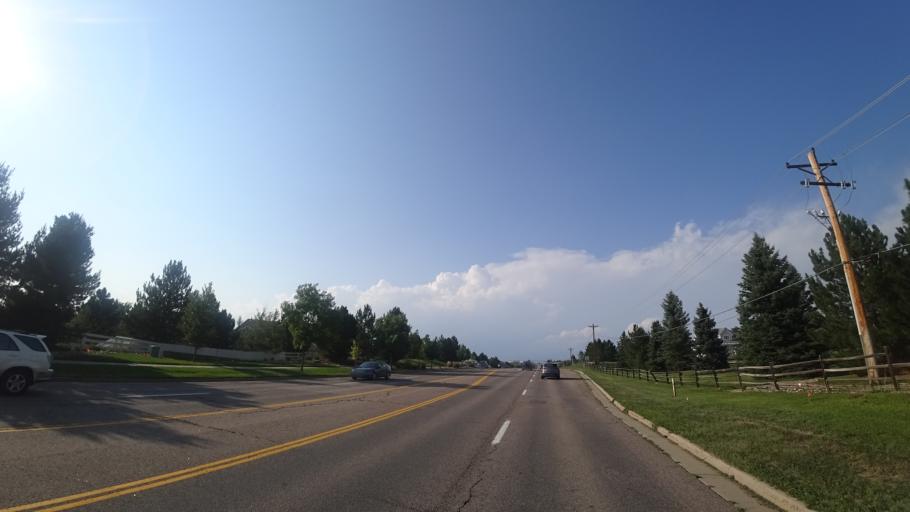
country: US
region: Colorado
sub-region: Douglas County
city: Parker
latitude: 39.5990
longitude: -104.7448
